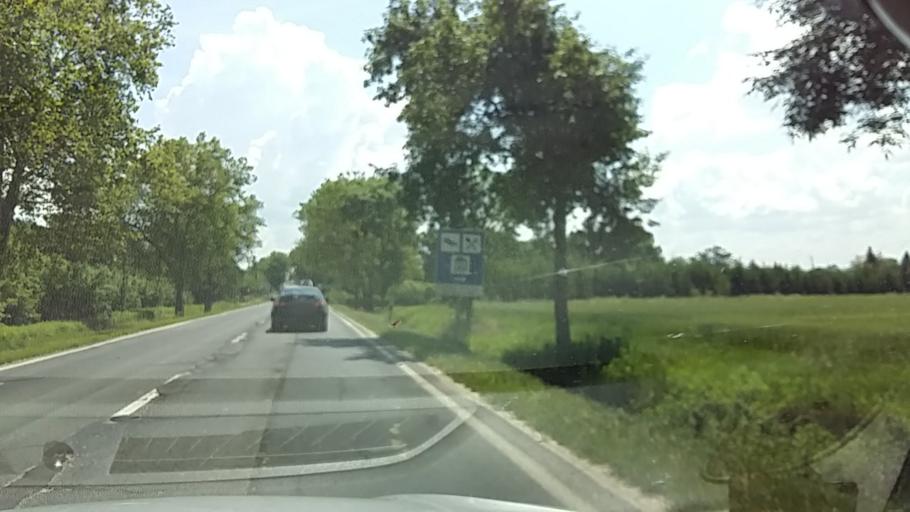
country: AT
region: Burgenland
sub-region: Politischer Bezirk Gussing
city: Heiligenbrunn
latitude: 46.9684
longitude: 16.4229
